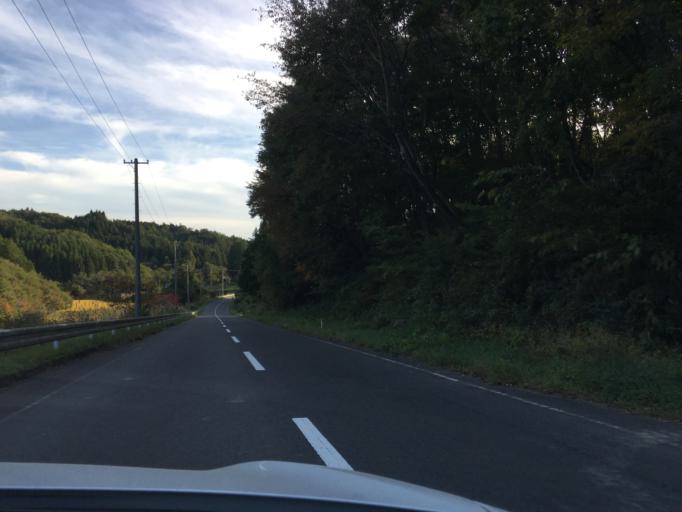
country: JP
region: Fukushima
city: Ishikawa
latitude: 37.2141
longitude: 140.5514
